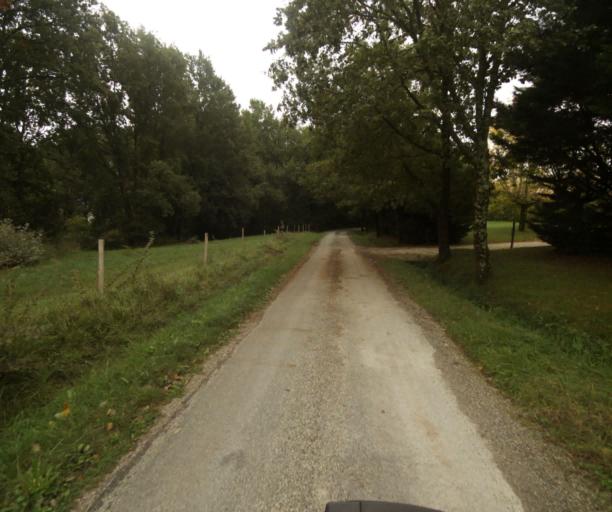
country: FR
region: Midi-Pyrenees
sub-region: Departement du Tarn-et-Garonne
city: Orgueil
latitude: 43.9095
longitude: 1.4120
